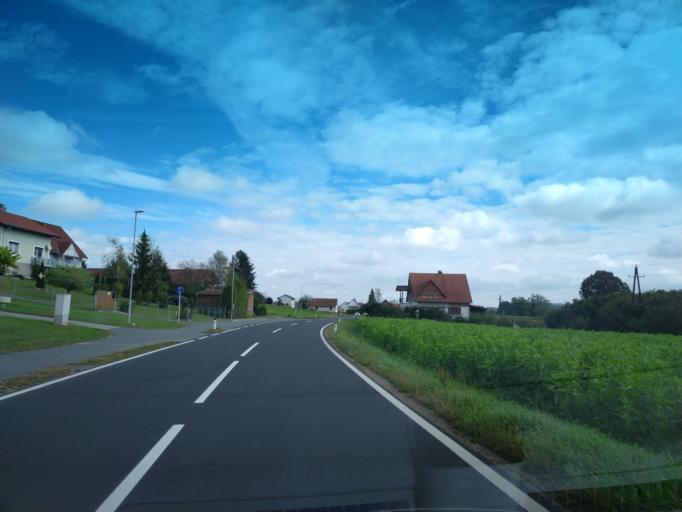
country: AT
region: Styria
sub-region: Politischer Bezirk Deutschlandsberg
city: Gross Sankt Florian
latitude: 46.8297
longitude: 15.3408
